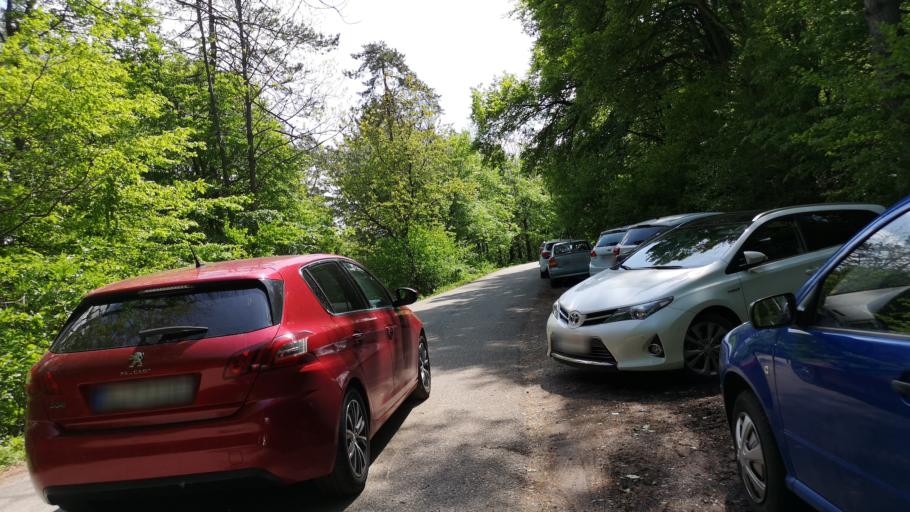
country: SK
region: Nitriansky
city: Brezova pod Bradlom
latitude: 48.6816
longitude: 17.5585
